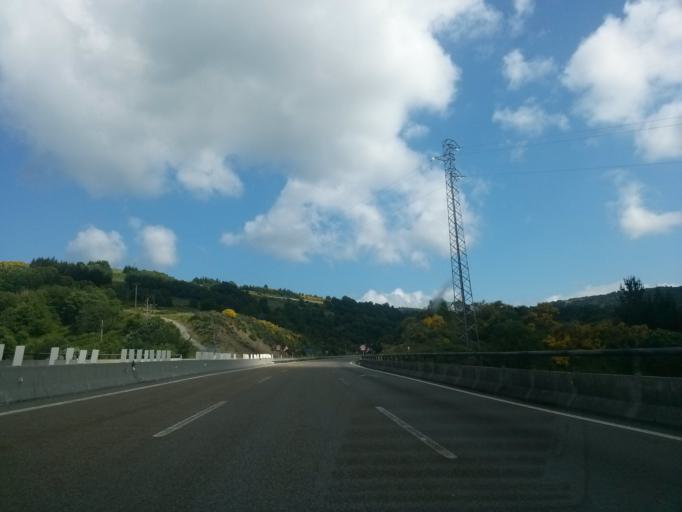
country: ES
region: Galicia
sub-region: Provincia de Lugo
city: San Roman
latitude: 42.7417
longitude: -7.0497
